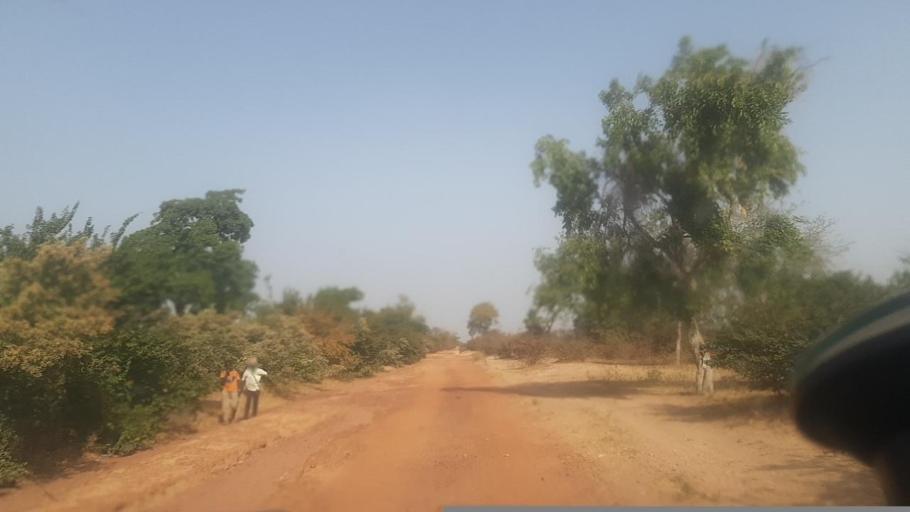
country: ML
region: Segou
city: Bla
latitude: 12.8549
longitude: -5.9770
